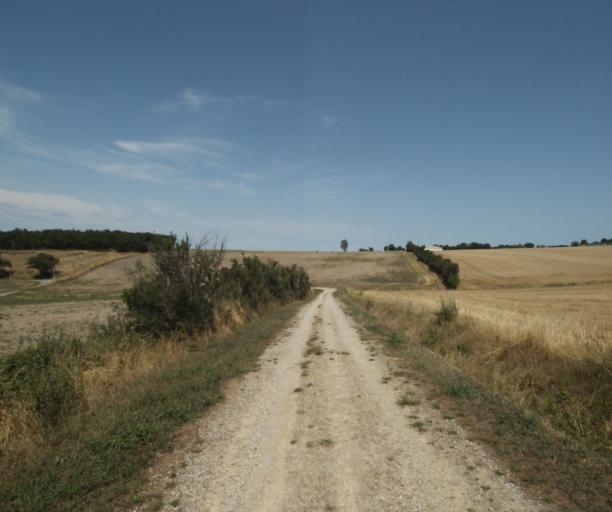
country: FR
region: Midi-Pyrenees
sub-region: Departement de la Haute-Garonne
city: Saint-Felix-Lauragais
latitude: 43.4521
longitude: 1.8507
